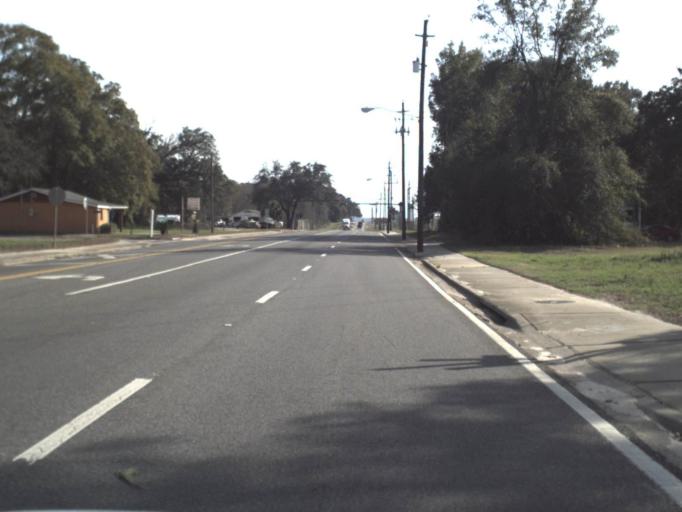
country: US
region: Florida
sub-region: Bay County
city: Springfield
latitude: 30.1477
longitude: -85.6157
